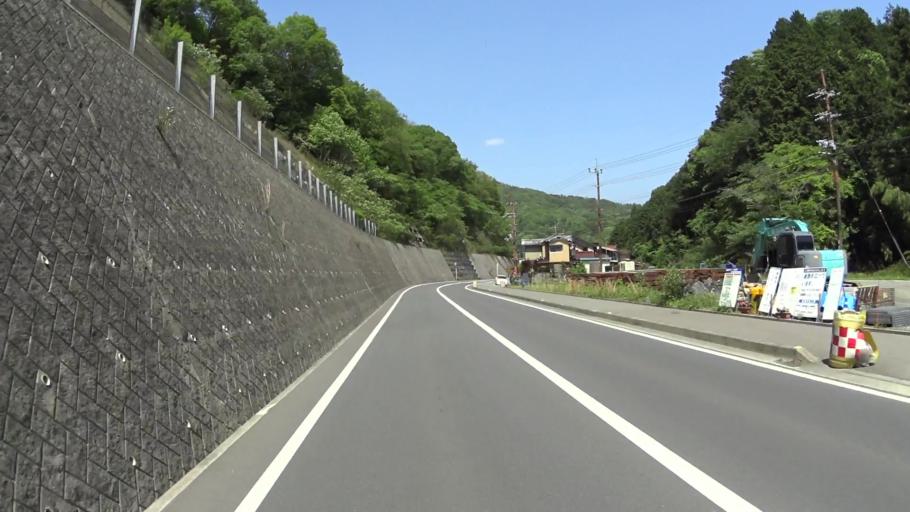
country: JP
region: Kyoto
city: Kameoka
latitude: 35.0234
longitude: 135.5069
